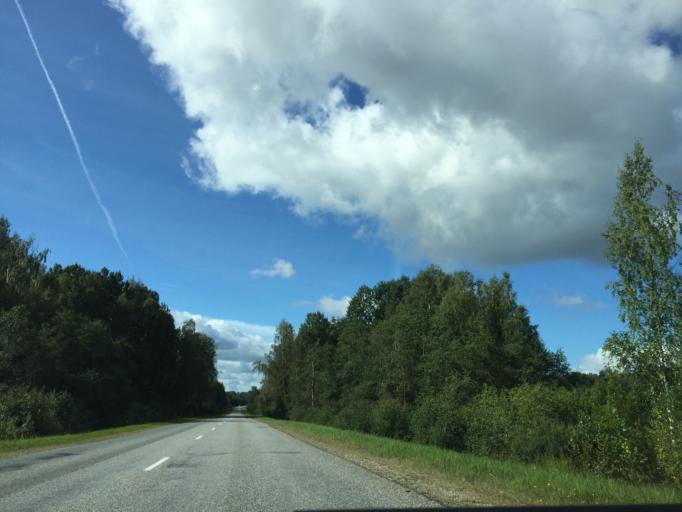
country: LV
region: Kuldigas Rajons
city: Kuldiga
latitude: 56.9913
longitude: 22.0845
